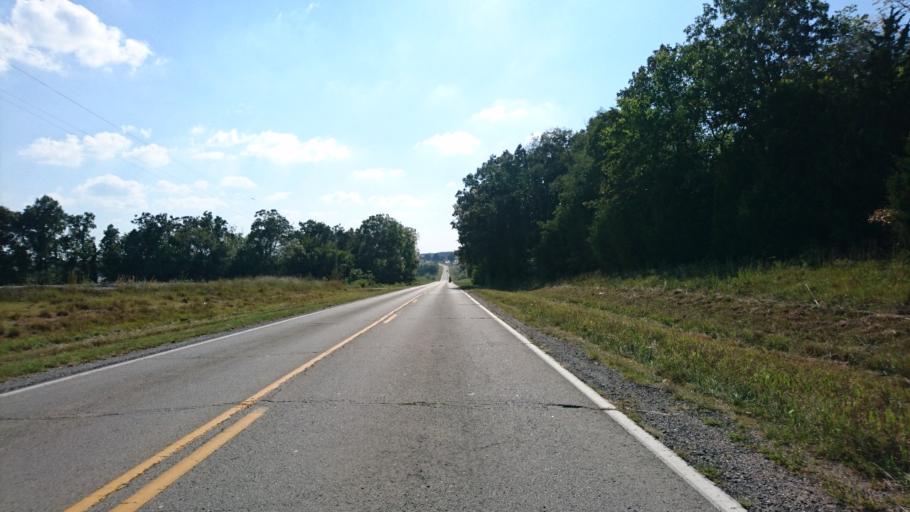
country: US
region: Missouri
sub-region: Laclede County
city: Lebanon
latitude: 37.6383
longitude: -92.6782
